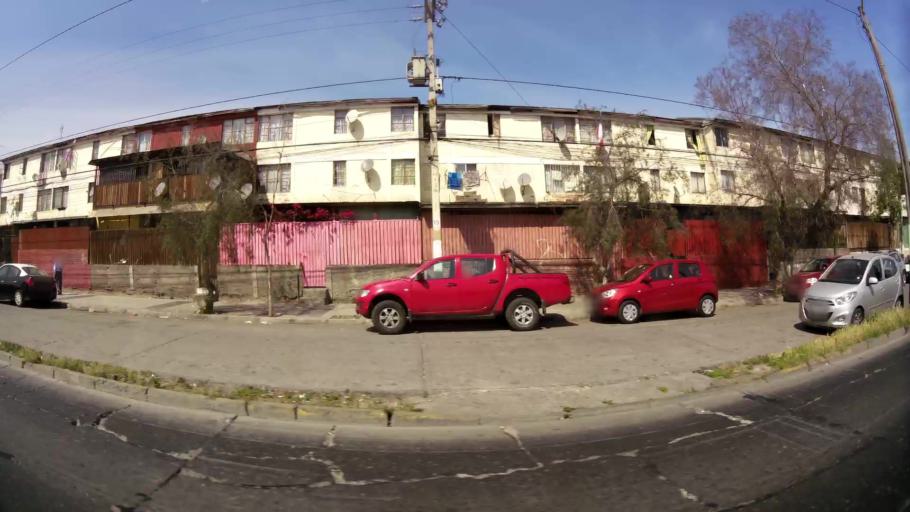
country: CL
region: Santiago Metropolitan
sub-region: Provincia de Santiago
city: Lo Prado
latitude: -33.4447
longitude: -70.7394
